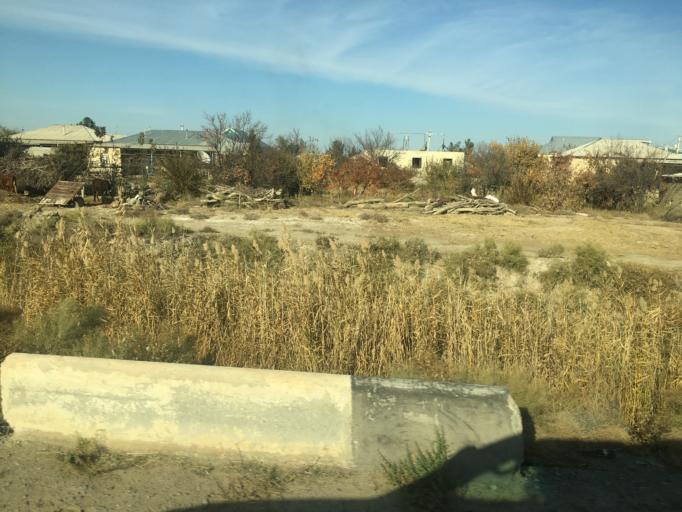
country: TM
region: Mary
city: Mary
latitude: 37.5897
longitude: 61.7733
